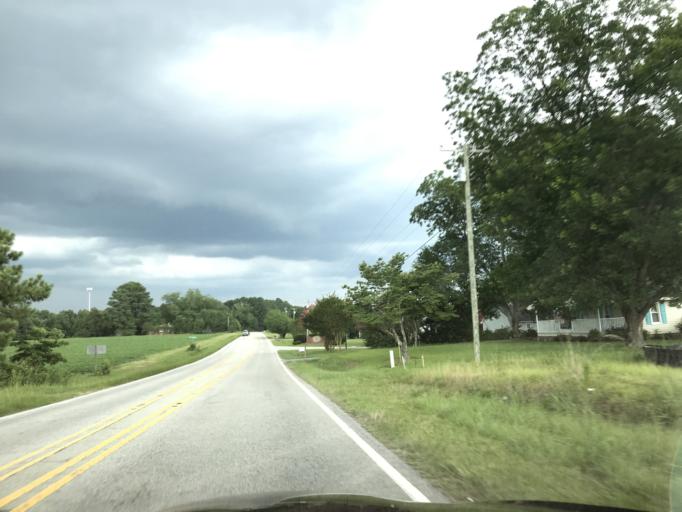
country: US
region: North Carolina
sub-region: Johnston County
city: Four Oaks
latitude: 35.5135
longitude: -78.5052
